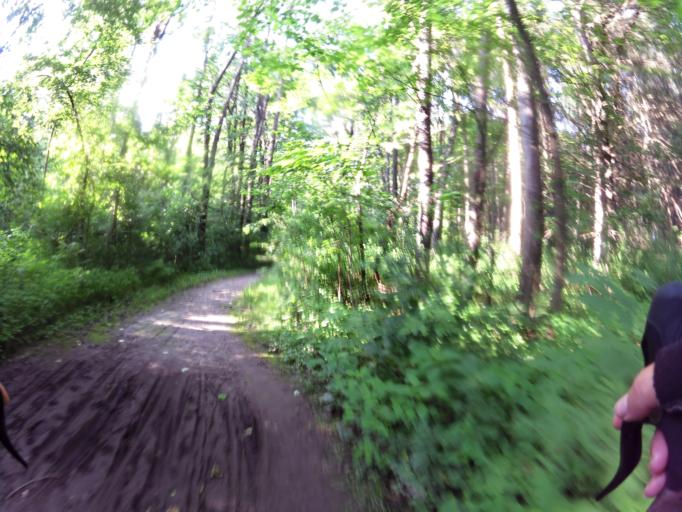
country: CA
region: Ontario
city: Ottawa
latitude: 45.3258
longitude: -75.7285
